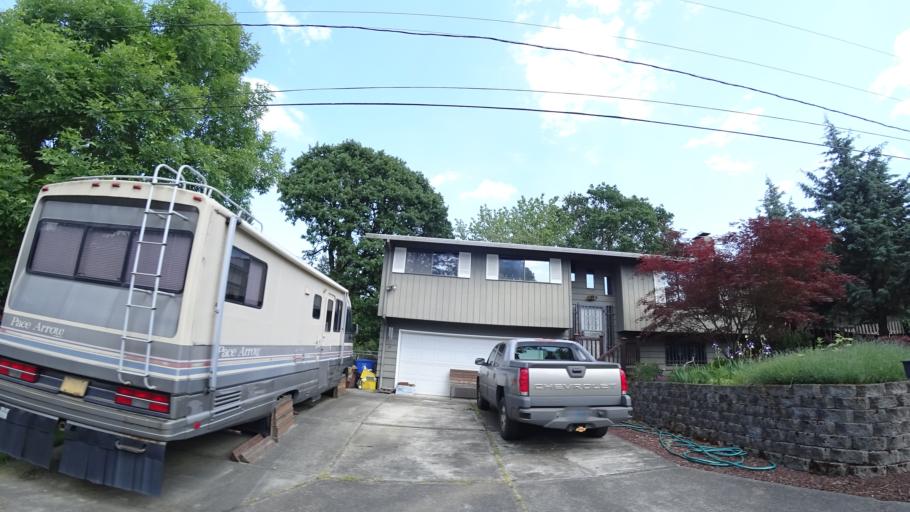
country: US
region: Oregon
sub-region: Washington County
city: Metzger
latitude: 45.4474
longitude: -122.7367
